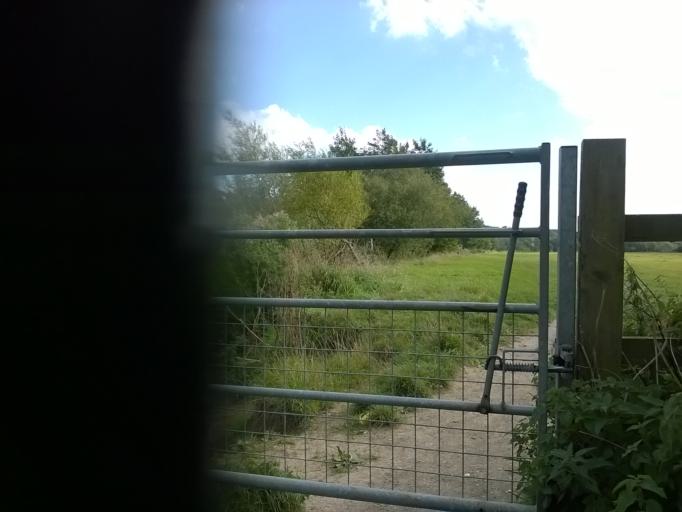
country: GB
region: England
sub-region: West Berkshire
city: Pangbourne
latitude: 51.4920
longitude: -1.0579
